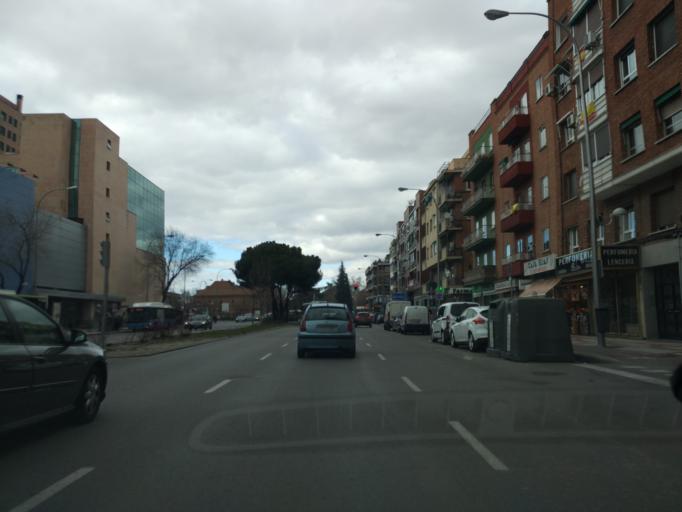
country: ES
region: Madrid
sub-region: Provincia de Madrid
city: Ciudad Lineal
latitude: 40.4368
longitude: -3.6371
